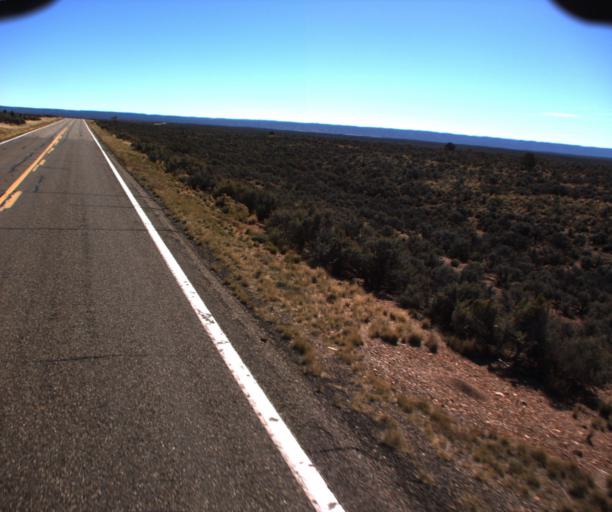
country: US
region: Arizona
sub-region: Coconino County
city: Fredonia
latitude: 36.9061
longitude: -112.3925
